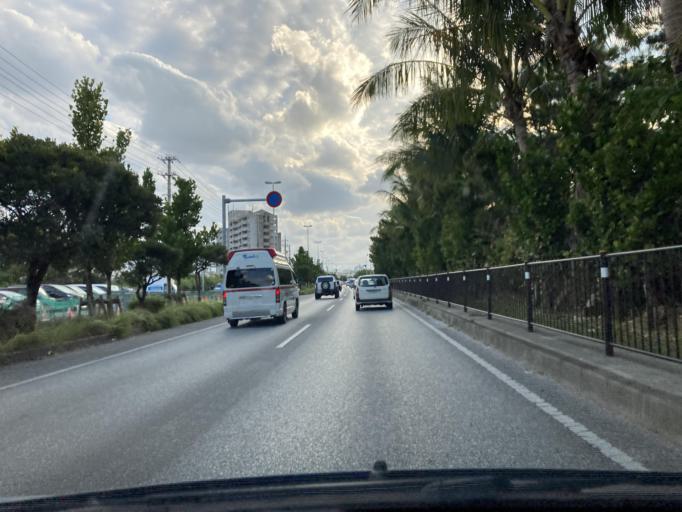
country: JP
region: Okinawa
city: Ginowan
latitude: 26.2830
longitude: 127.7439
